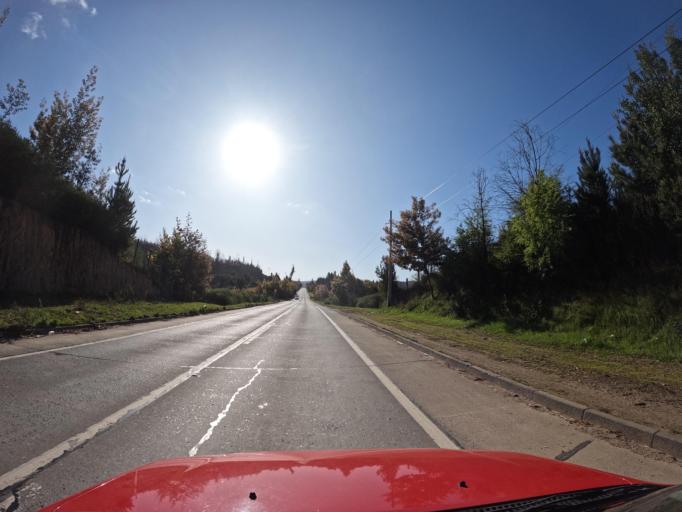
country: CL
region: Maule
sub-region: Provincia de Talca
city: Constitucion
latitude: -35.4657
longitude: -72.2532
